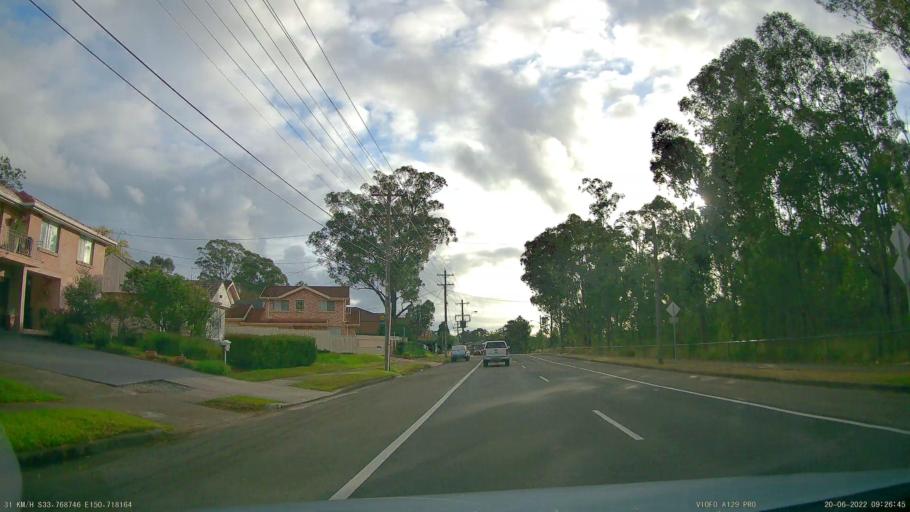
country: AU
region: New South Wales
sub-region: Penrith Municipality
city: Kingswood Park
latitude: -33.7686
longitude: 150.7183
